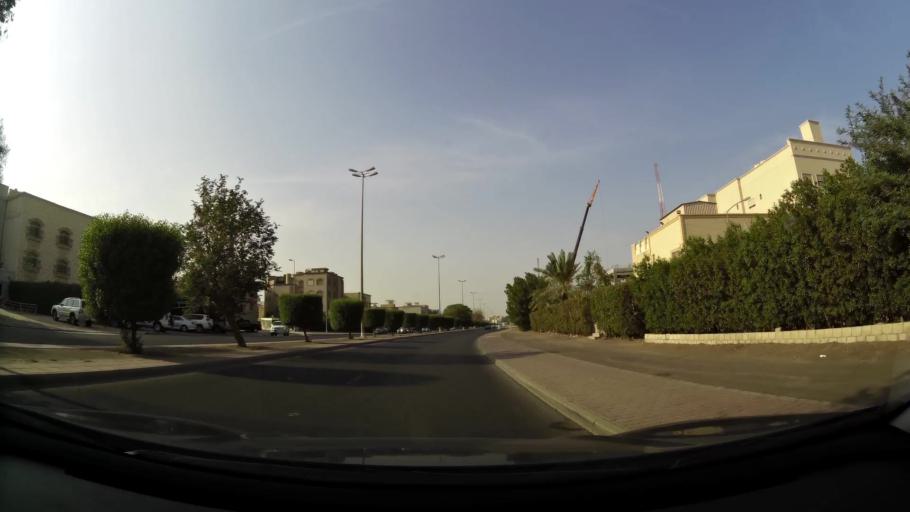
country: KW
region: Mubarak al Kabir
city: Mubarak al Kabir
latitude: 29.1674
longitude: 48.0801
